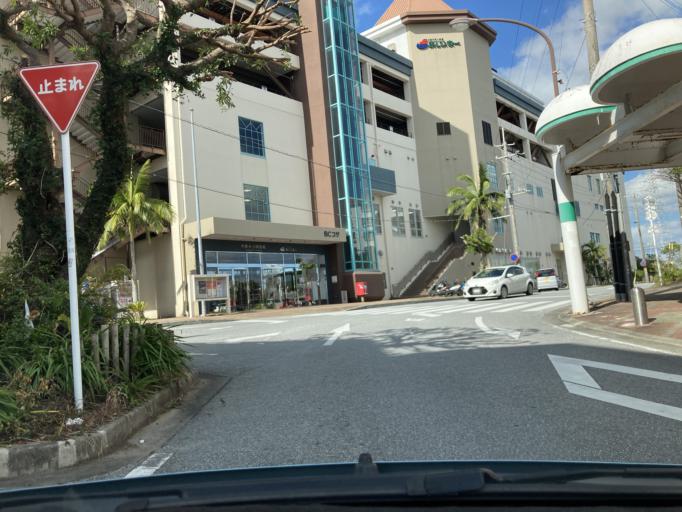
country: JP
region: Okinawa
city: Okinawa
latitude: 26.3403
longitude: 127.7990
